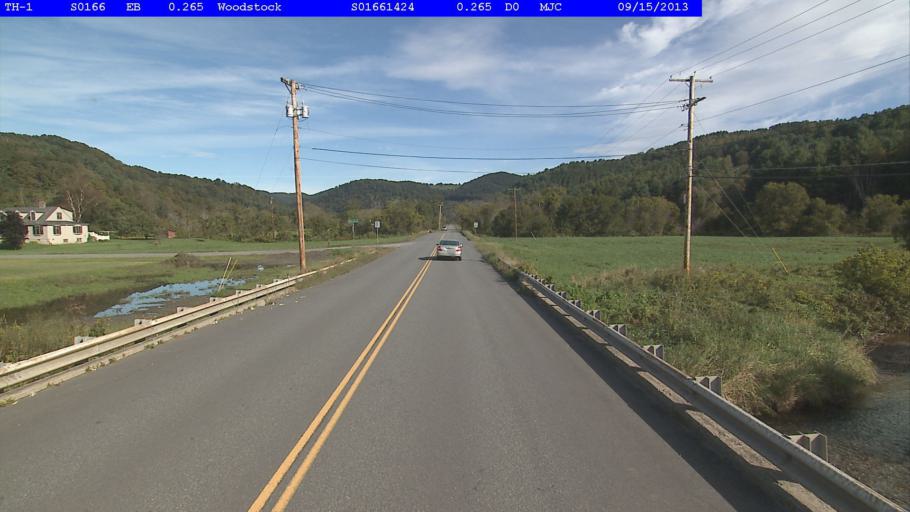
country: US
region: Vermont
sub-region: Windsor County
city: Woodstock
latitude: 43.6421
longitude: -72.5255
